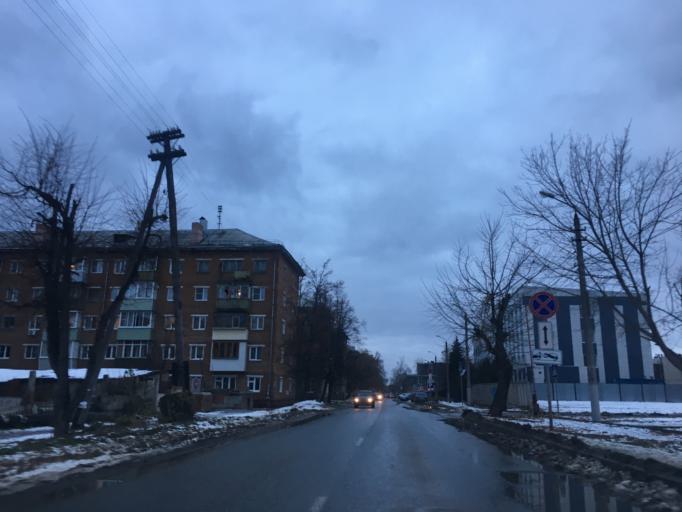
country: RU
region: Tula
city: Tula
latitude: 54.1989
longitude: 37.5989
